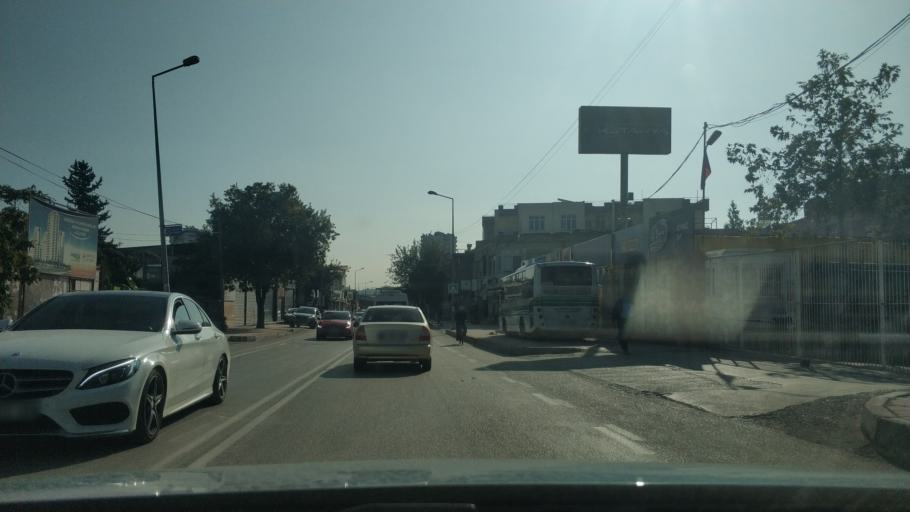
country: TR
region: Adana
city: Seyhan
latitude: 37.0148
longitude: 35.3019
